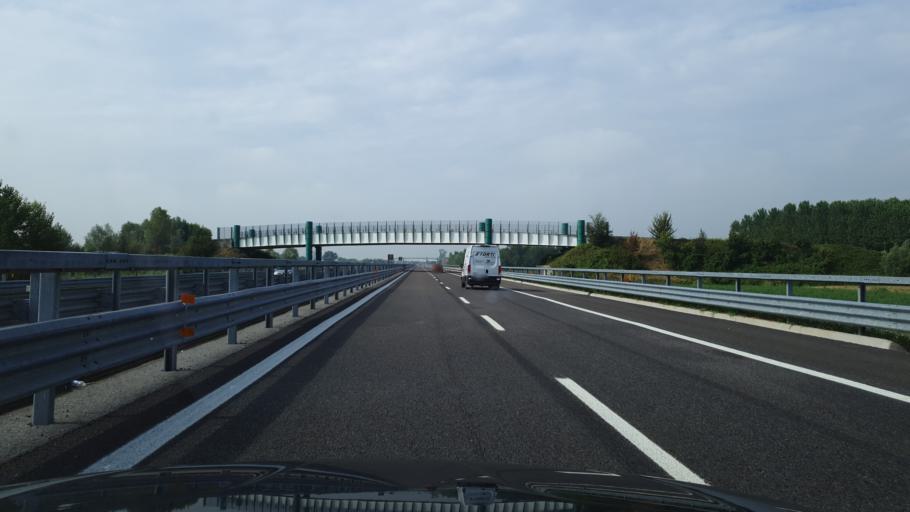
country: IT
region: Veneto
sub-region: Provincia di Padova
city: Megliadino San Vitale
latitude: 45.1863
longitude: 11.5396
